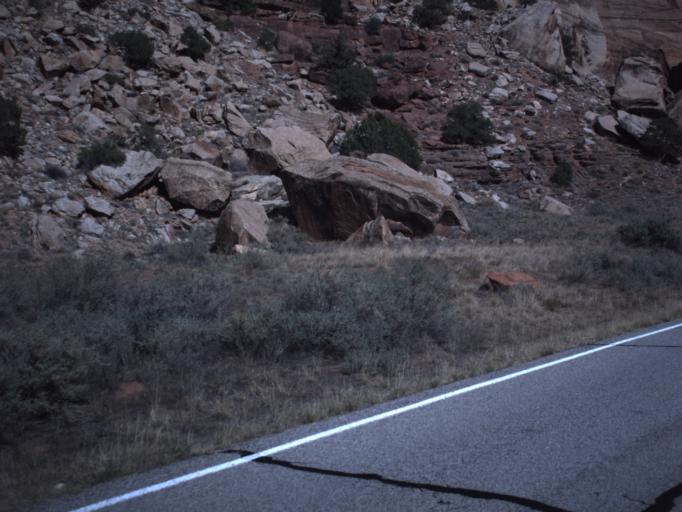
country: US
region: Utah
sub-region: San Juan County
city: Monticello
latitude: 38.0333
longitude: -109.5431
